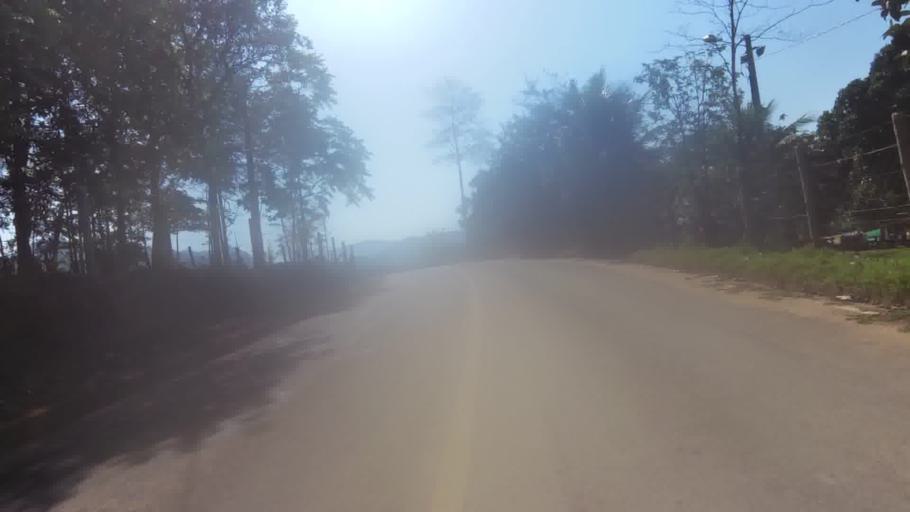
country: BR
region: Espirito Santo
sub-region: Alfredo Chaves
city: Alfredo Chaves
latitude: -20.6648
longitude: -40.7652
